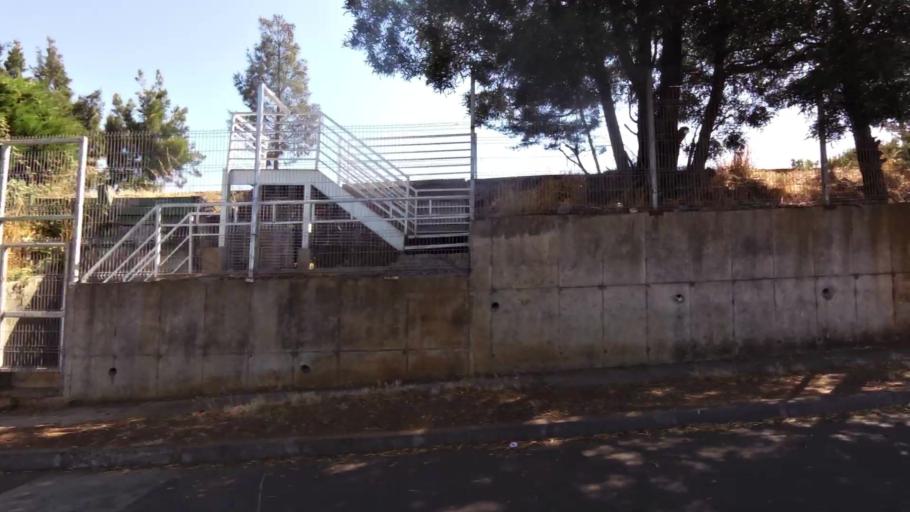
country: CL
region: Biobio
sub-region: Provincia de Concepcion
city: Concepcion
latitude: -36.7843
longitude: -73.0504
